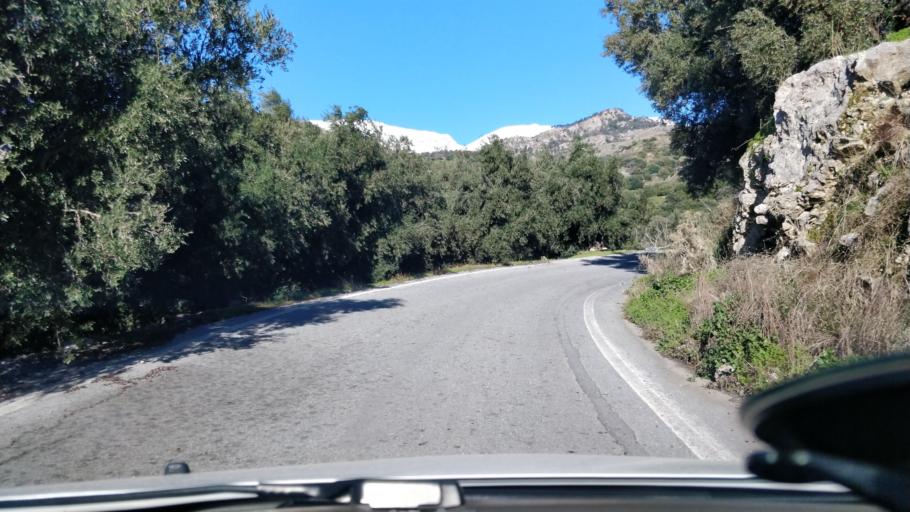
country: GR
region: Crete
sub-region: Nomos Lasithiou
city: Kritsa
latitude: 35.0755
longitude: 25.5836
